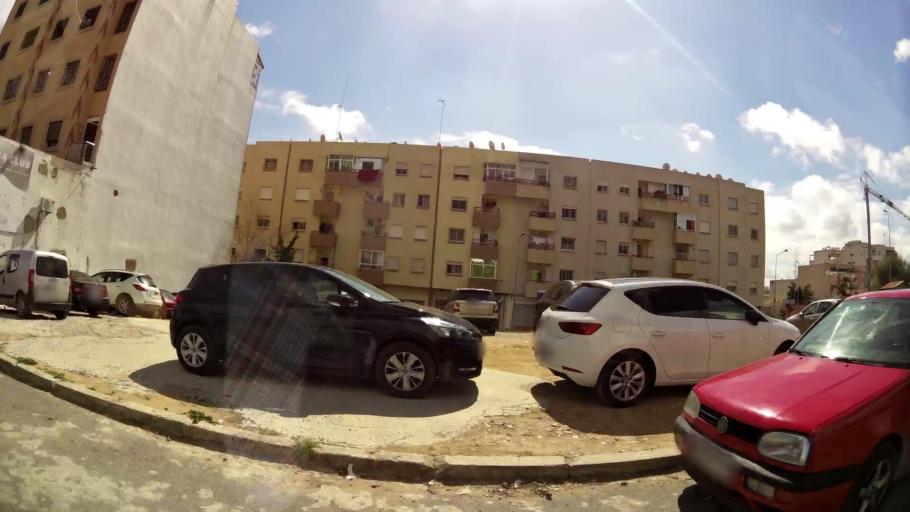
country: MA
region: Tanger-Tetouan
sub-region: Tanger-Assilah
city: Tangier
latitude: 35.7726
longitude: -5.8315
